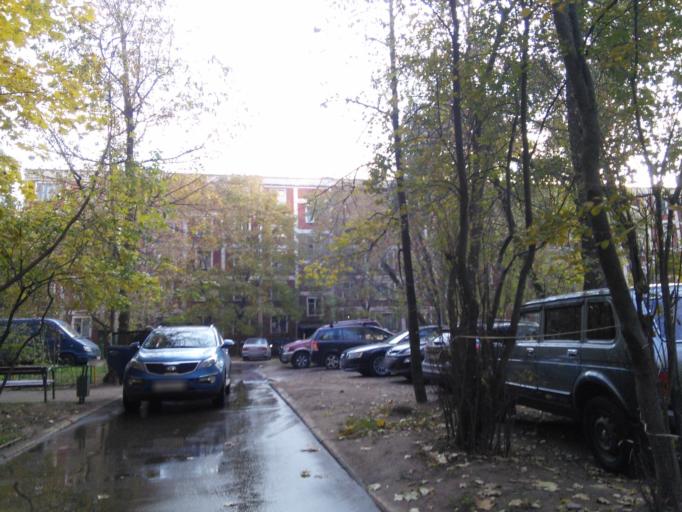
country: RU
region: Moskovskaya
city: Khoroshevo-Mnevniki
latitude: 55.7724
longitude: 37.4715
